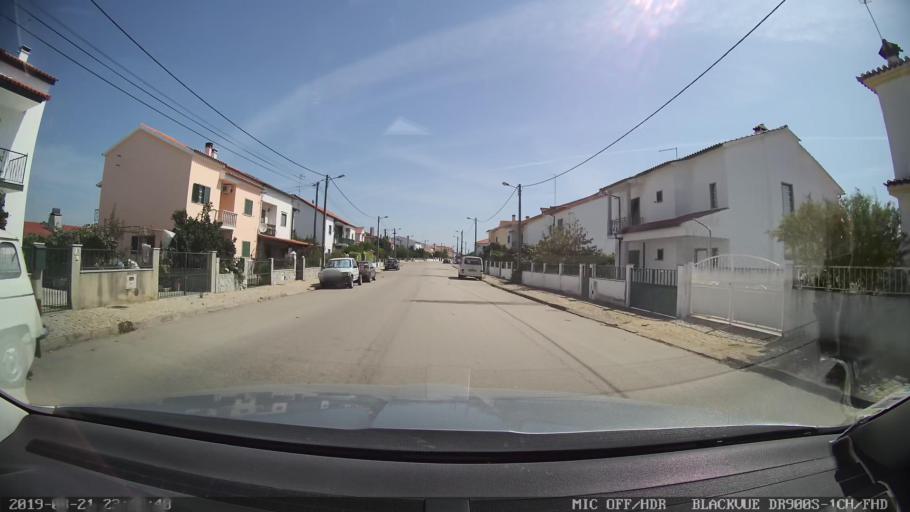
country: PT
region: Castelo Branco
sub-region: Idanha-A-Nova
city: Idanha-a-Nova
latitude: 39.8386
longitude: -7.2630
